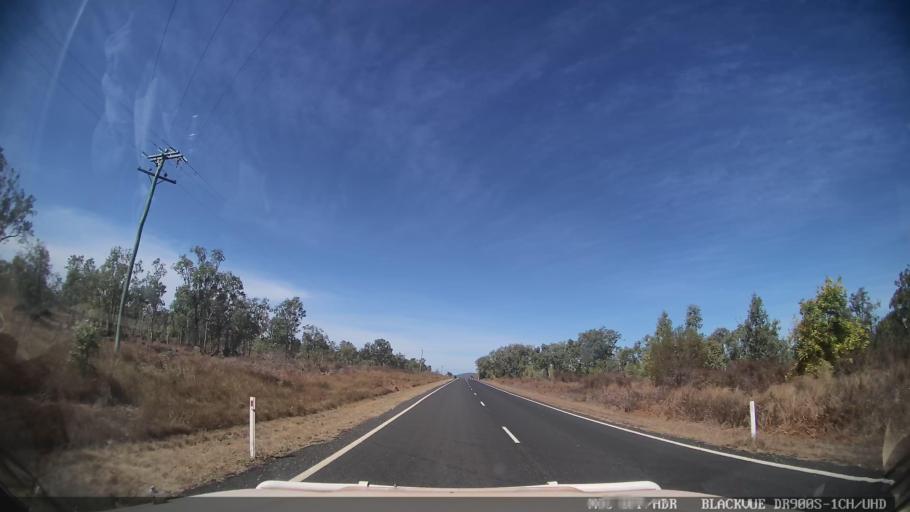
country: AU
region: Queensland
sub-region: Cook
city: Cooktown
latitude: -15.8657
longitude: 144.8112
